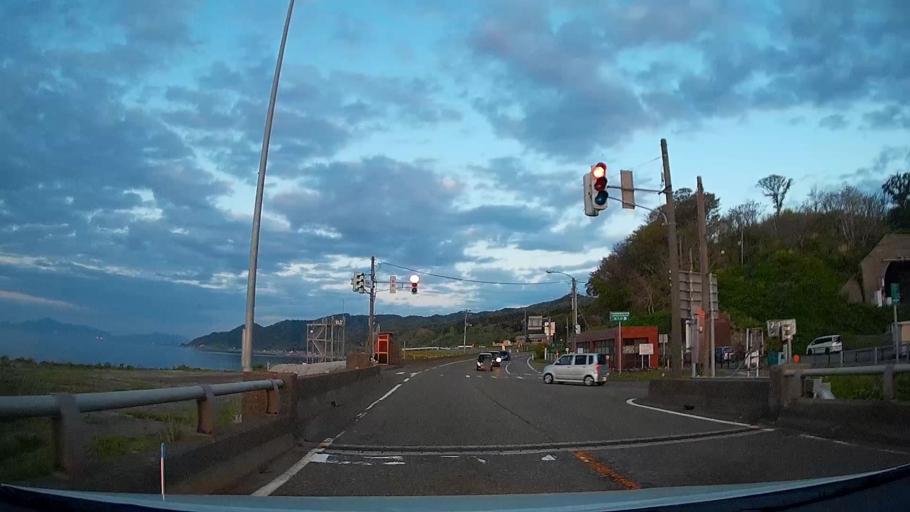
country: JP
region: Niigata
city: Joetsu
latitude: 37.1632
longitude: 138.1466
